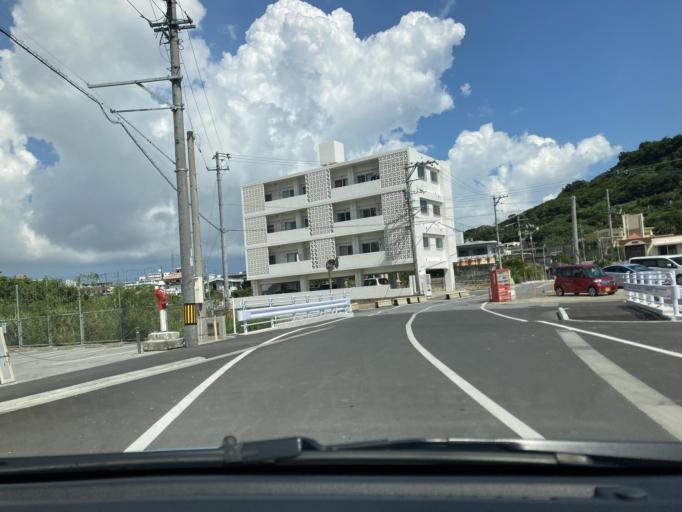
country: JP
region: Okinawa
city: Tomigusuku
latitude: 26.1621
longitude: 127.7566
